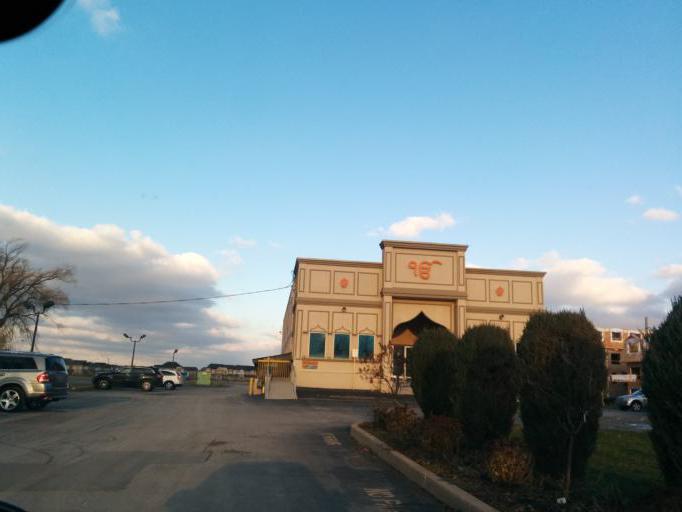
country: CA
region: Ontario
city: Burlington
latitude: 43.4331
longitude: -79.7720
